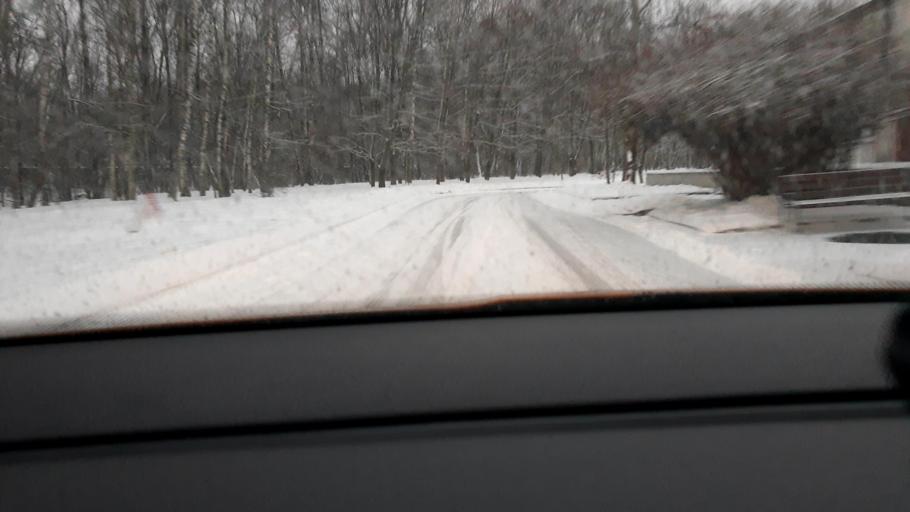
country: RU
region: Moskovskaya
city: Nemchinovka
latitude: 55.7562
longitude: 37.3808
